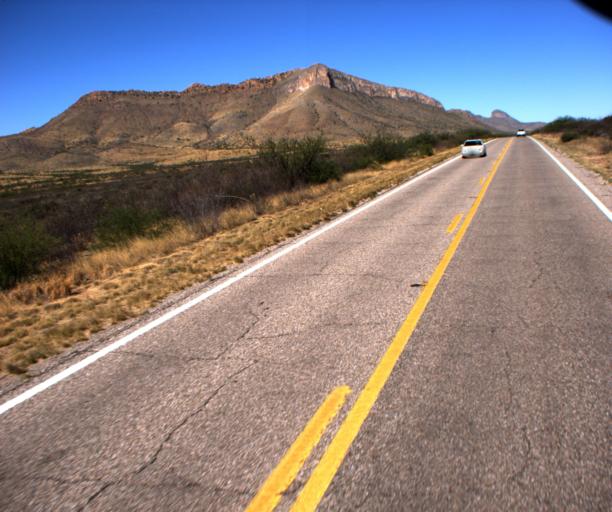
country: US
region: Arizona
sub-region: Cochise County
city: Huachuca City
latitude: 31.6924
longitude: -110.4048
